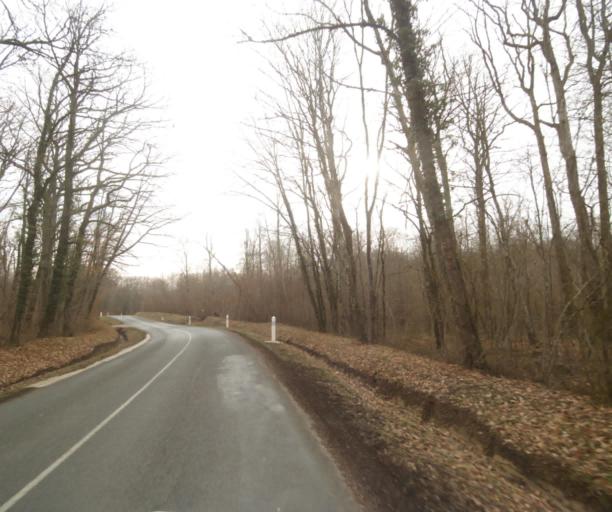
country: FR
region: Champagne-Ardenne
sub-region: Departement de la Marne
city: Pargny-sur-Saulx
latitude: 48.7308
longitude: 4.8654
